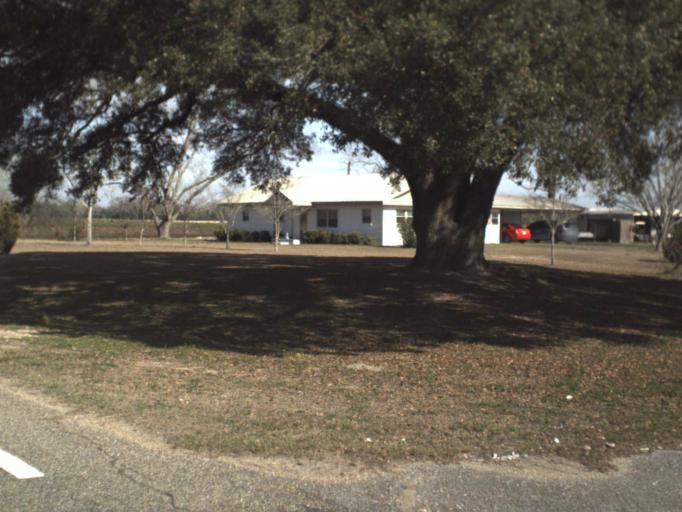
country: US
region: Florida
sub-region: Jackson County
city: Malone
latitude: 30.9788
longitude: -85.1748
